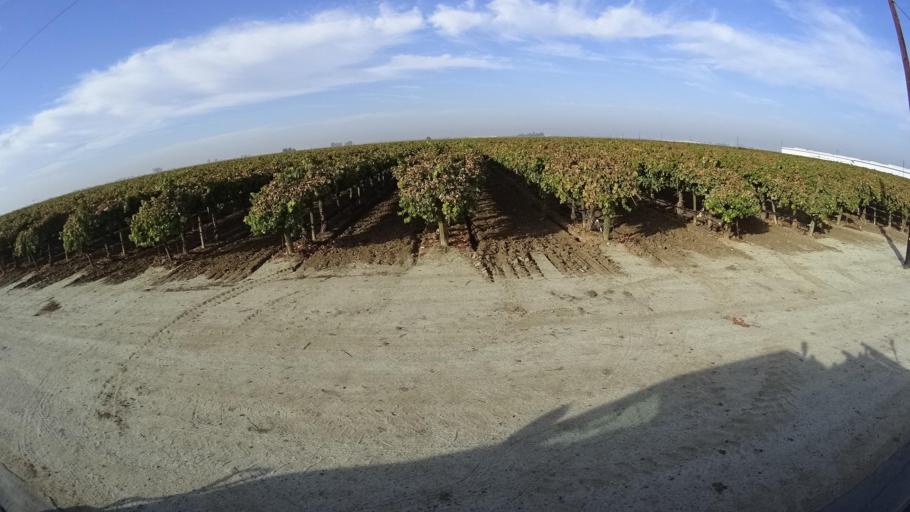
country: US
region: California
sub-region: Kern County
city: McFarland
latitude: 35.7006
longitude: -119.2049
